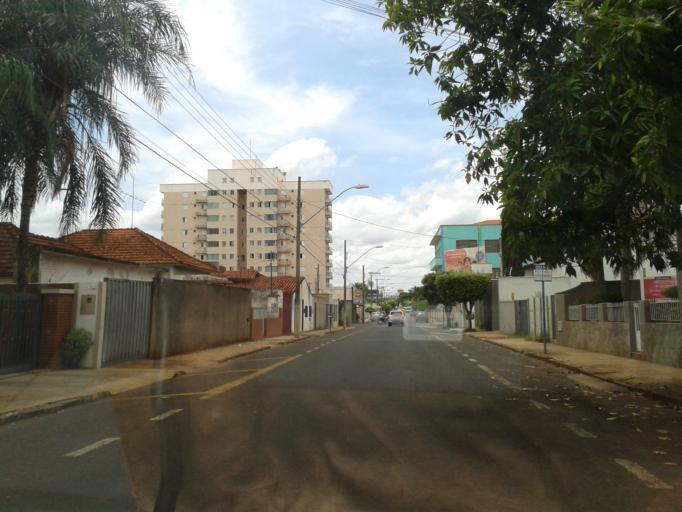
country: BR
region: Minas Gerais
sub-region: Ituiutaba
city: Ituiutaba
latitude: -18.9703
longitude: -49.4654
